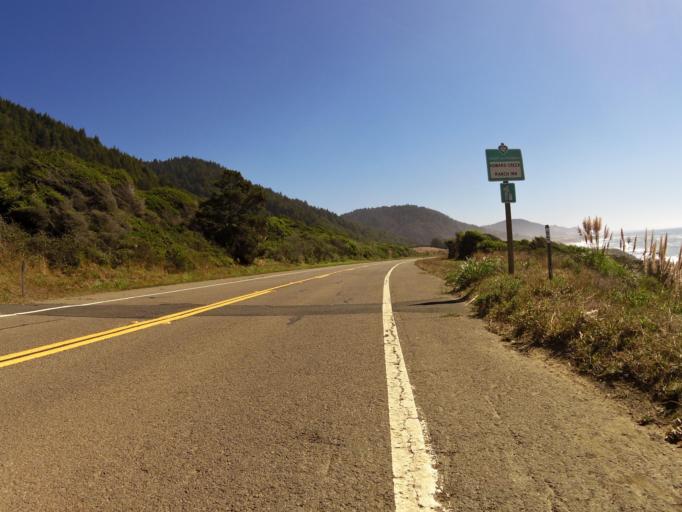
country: US
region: California
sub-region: Mendocino County
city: Fort Bragg
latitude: 39.6905
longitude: -123.7939
